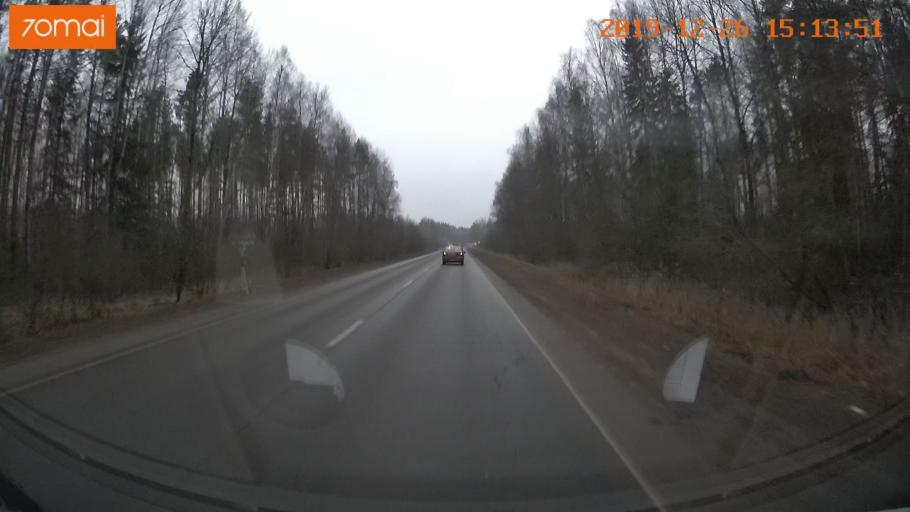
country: RU
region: Jaroslavl
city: Rybinsk
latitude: 58.1119
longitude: 38.8825
